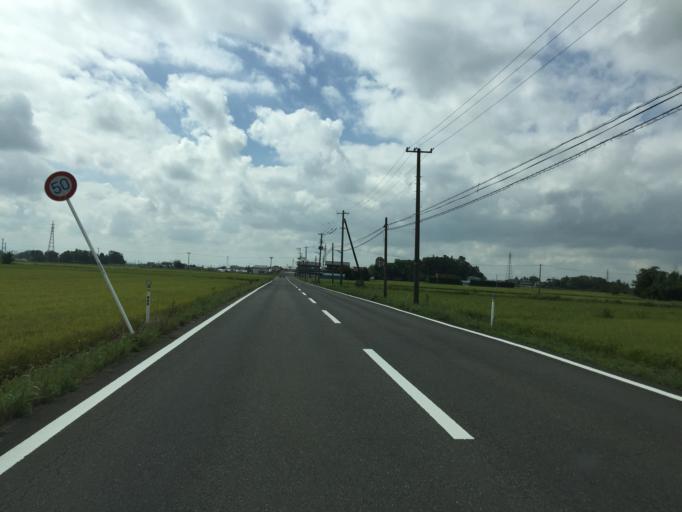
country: JP
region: Fukushima
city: Motomiya
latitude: 37.4716
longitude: 140.3404
